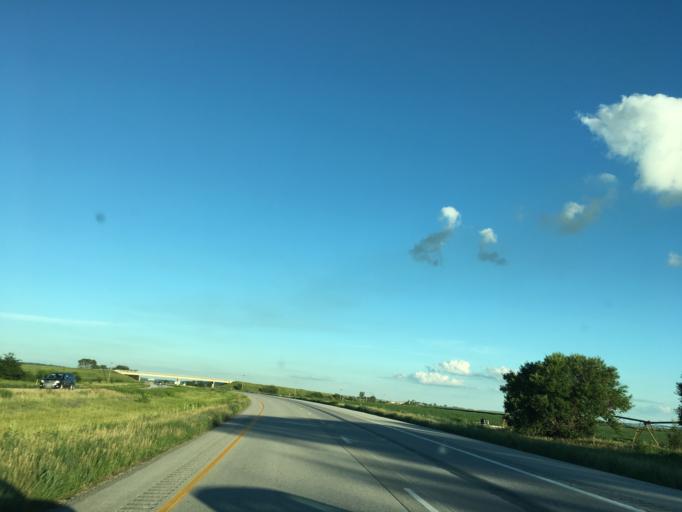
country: US
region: Iowa
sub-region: Fremont County
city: Hamburg
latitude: 40.6426
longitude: -95.7410
